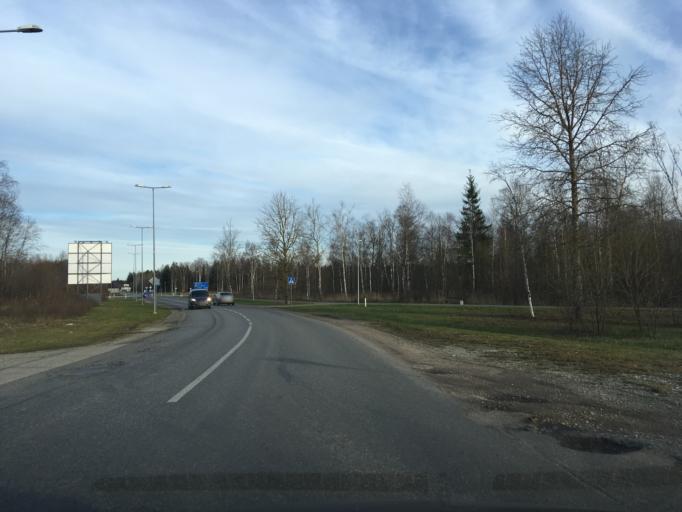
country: EE
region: Ida-Virumaa
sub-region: Johvi vald
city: Johvi
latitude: 59.3665
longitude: 27.4170
